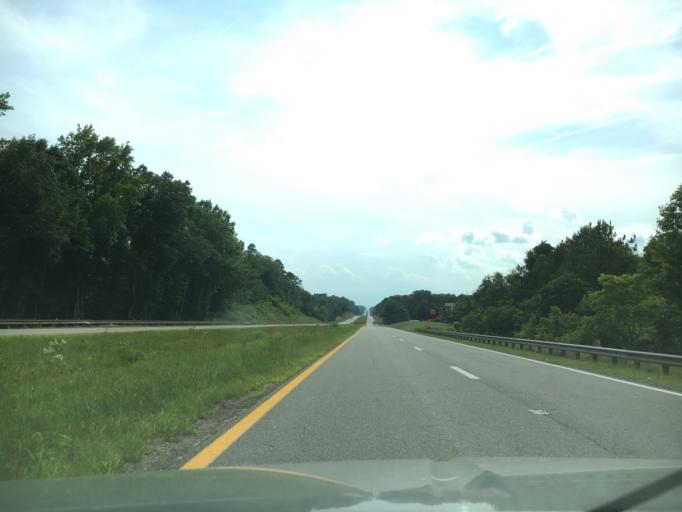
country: US
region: Virginia
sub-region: Mecklenburg County
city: Chase City
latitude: 36.8328
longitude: -78.6648
